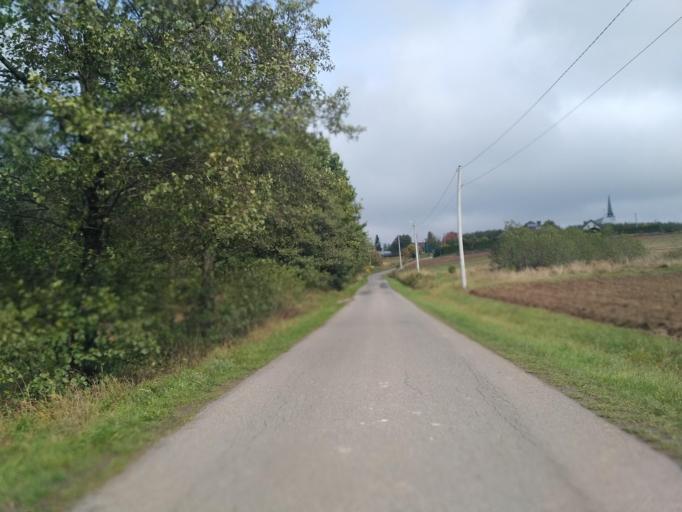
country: PL
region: Subcarpathian Voivodeship
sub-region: Powiat ropczycko-sedziszowski
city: Niedzwiada
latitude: 49.9609
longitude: 21.4422
